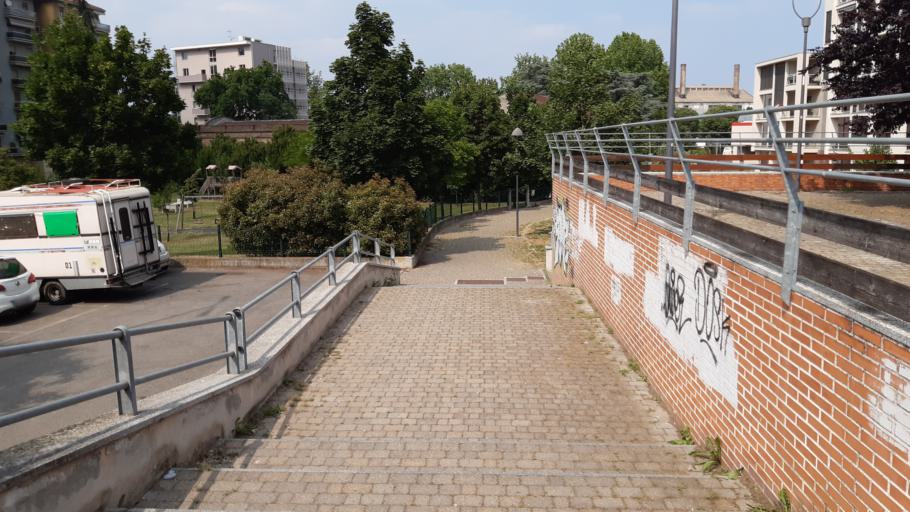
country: IT
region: Emilia-Romagna
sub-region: Provincia di Piacenza
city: Piacenza
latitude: 45.0545
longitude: 9.7015
